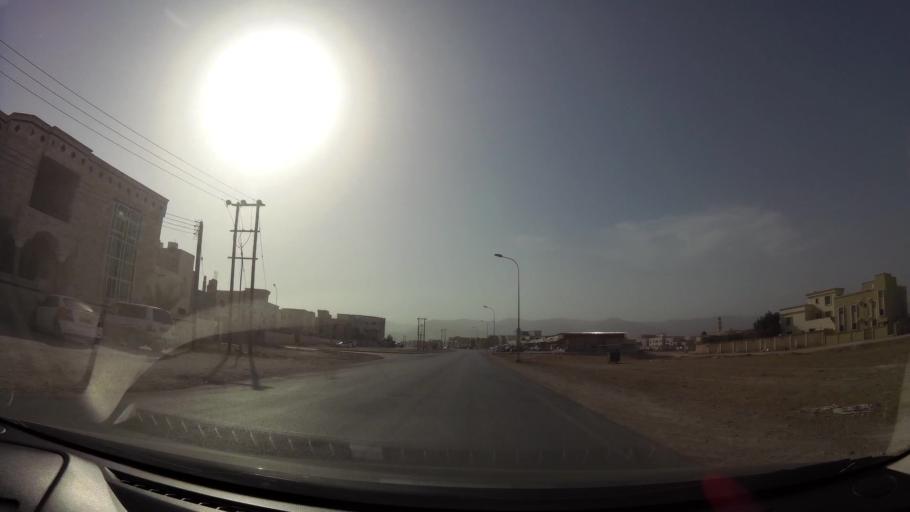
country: OM
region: Zufar
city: Salalah
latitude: 17.0103
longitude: 54.0187
